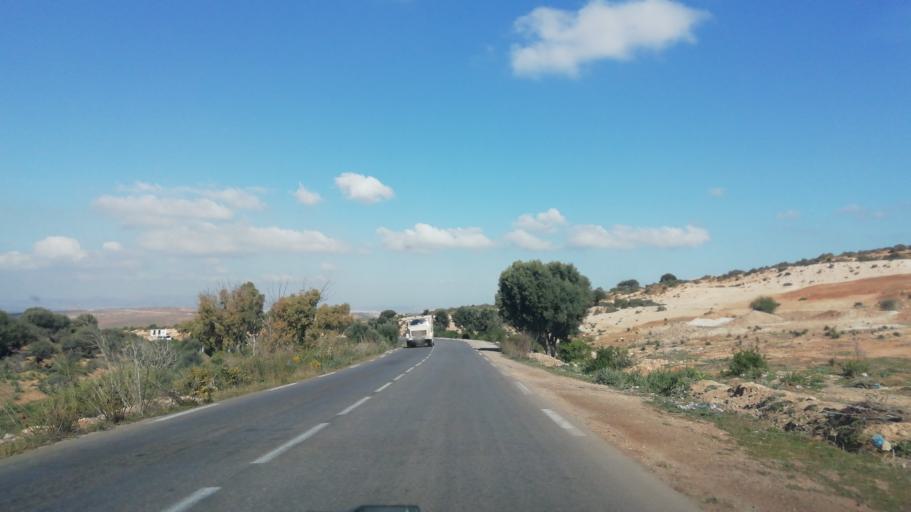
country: DZ
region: Oran
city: Ain el Bya
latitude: 35.7262
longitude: -0.2461
